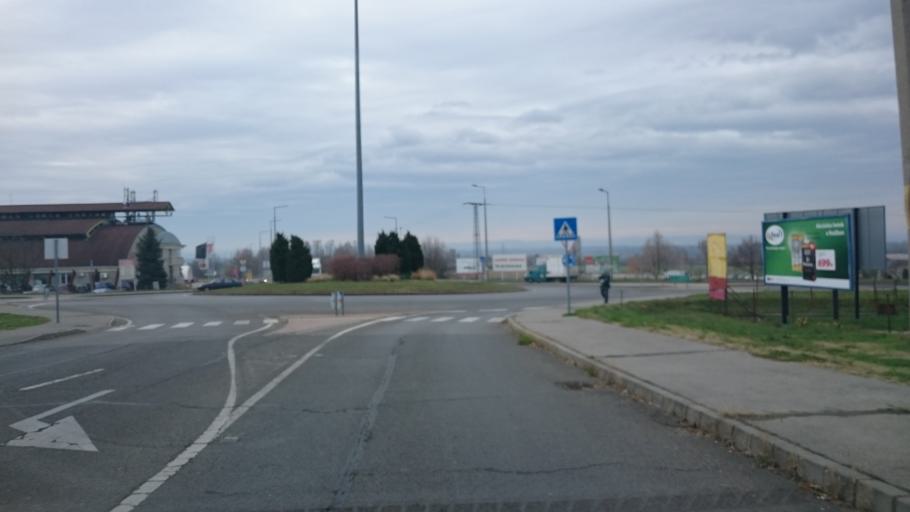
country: HU
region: Baranya
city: Pellerd
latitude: 46.0656
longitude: 18.1729
